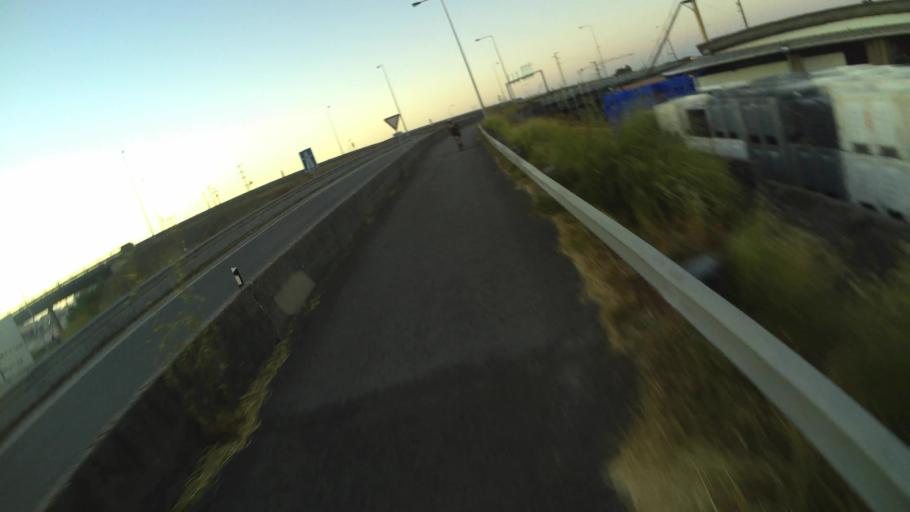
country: PT
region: Aveiro
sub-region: Ilhavo
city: Gafanha da Nazare
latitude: 40.6309
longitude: -8.6885
